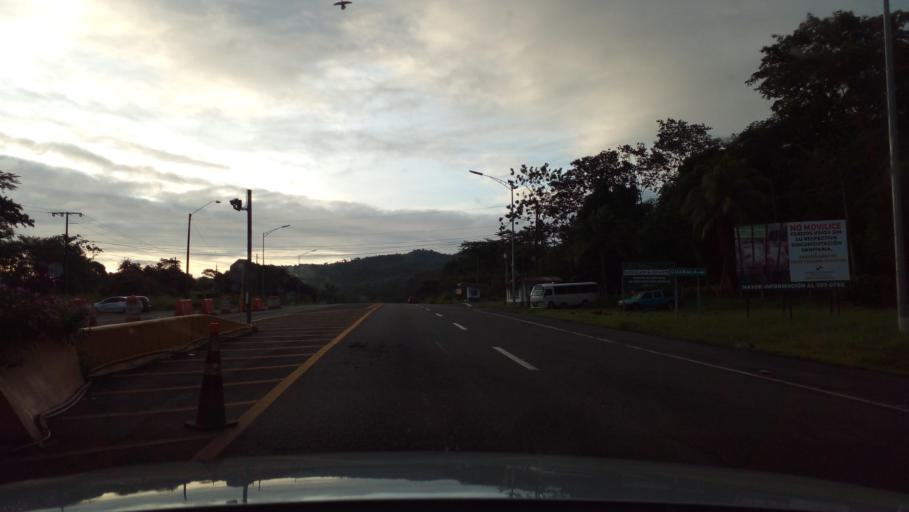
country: PA
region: Chiriqui
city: Pueblo Viejo
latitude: 8.2148
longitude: -81.7255
